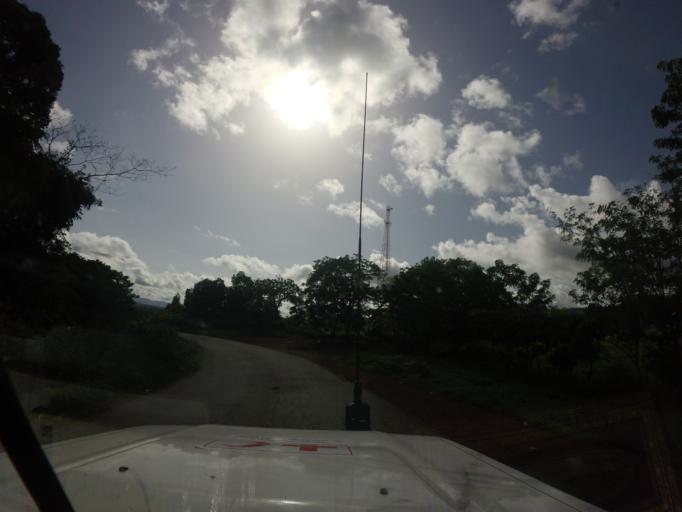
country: GN
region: Mamou
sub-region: Mamou Prefecture
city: Mamou
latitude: 10.3053
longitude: -12.2860
